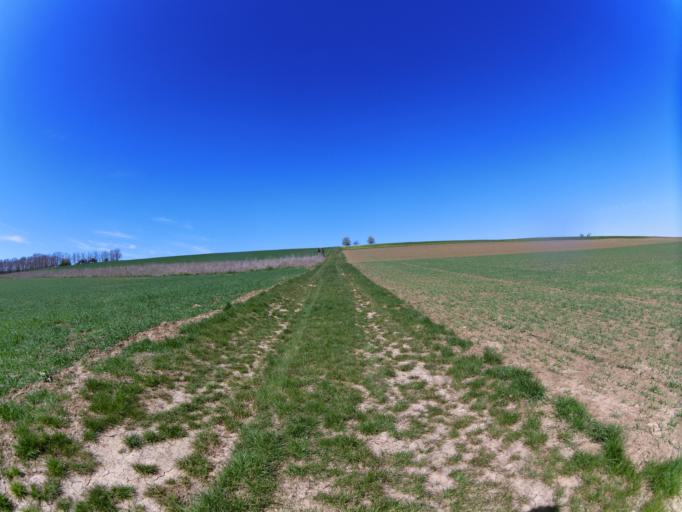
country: DE
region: Bavaria
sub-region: Regierungsbezirk Unterfranken
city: Winterhausen
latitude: 49.6930
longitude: 9.9940
